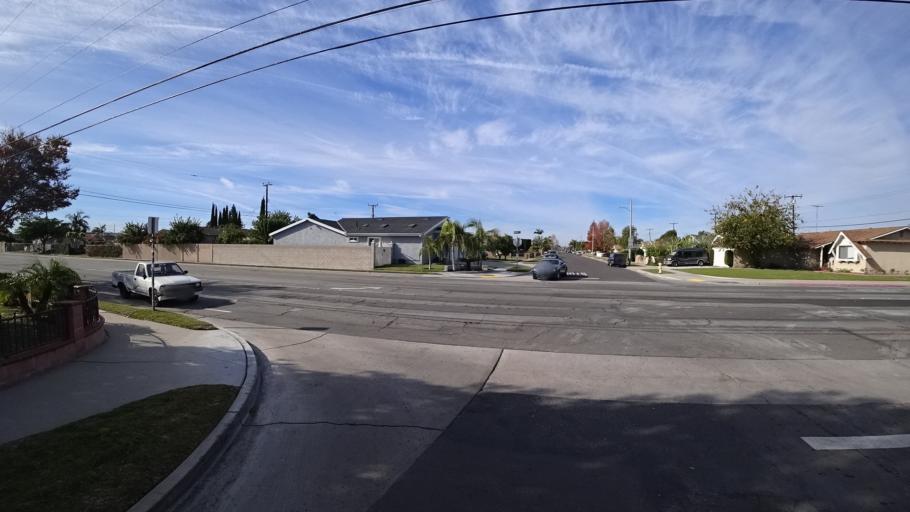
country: US
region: California
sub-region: Orange County
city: Garden Grove
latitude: 33.7482
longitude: -117.9460
